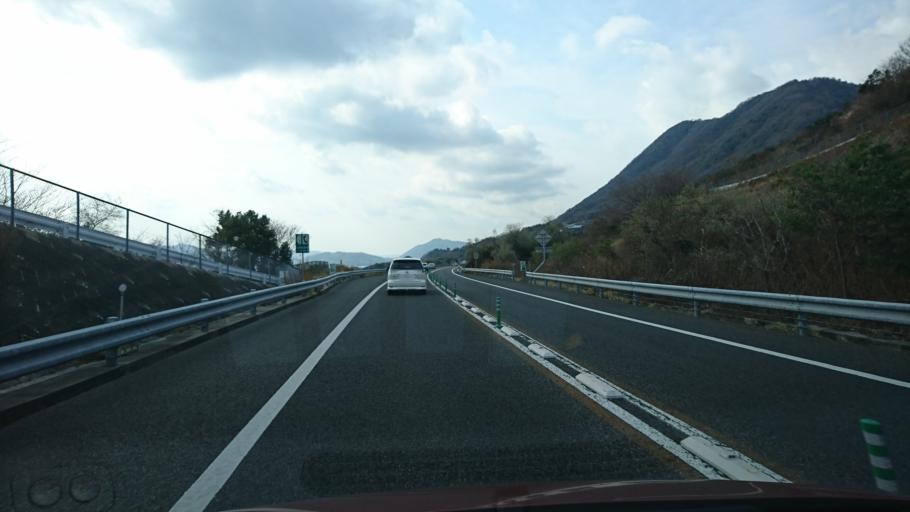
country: JP
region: Hiroshima
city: Innoshima
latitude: 34.2740
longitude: 133.1056
